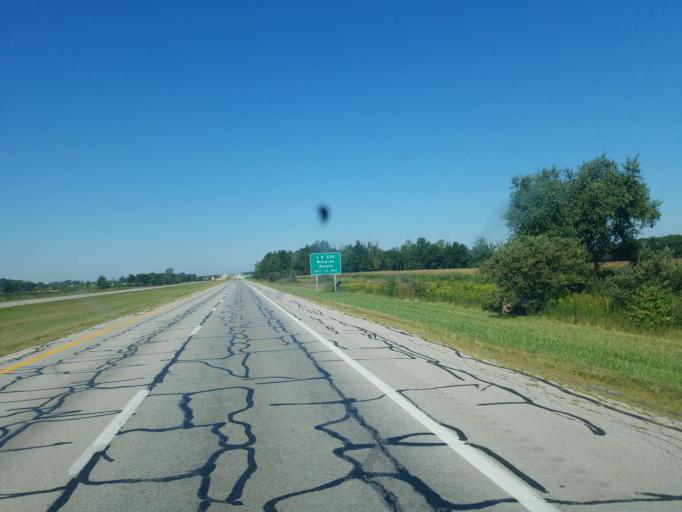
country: US
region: Ohio
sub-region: Crawford County
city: Bucyrus
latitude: 40.8275
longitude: -83.0186
